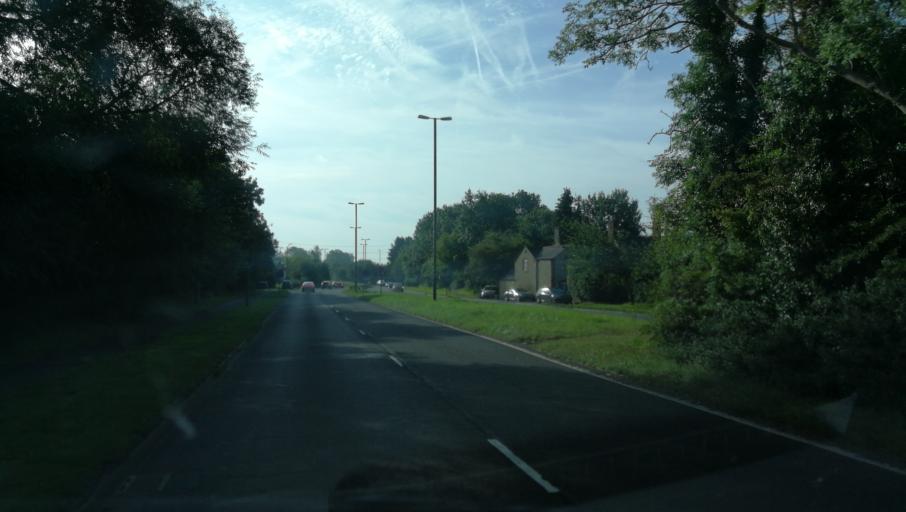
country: GB
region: England
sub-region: Oxfordshire
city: Yarnton
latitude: 51.8084
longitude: -1.3033
